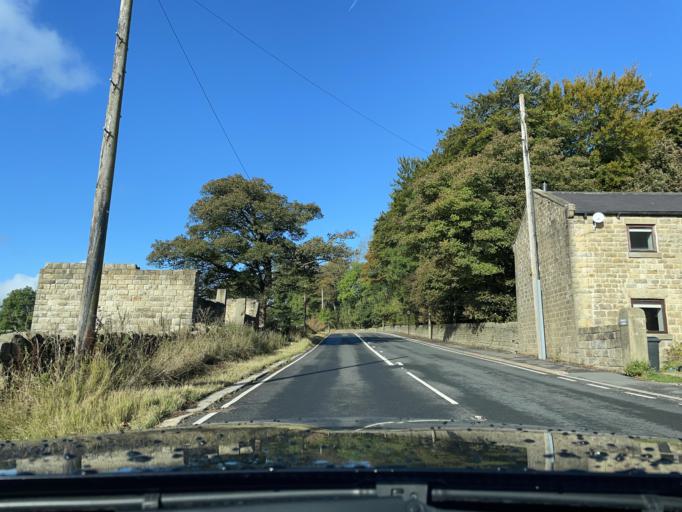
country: GB
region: England
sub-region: Sheffield
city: Bradfield
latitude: 53.3861
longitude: -1.6126
